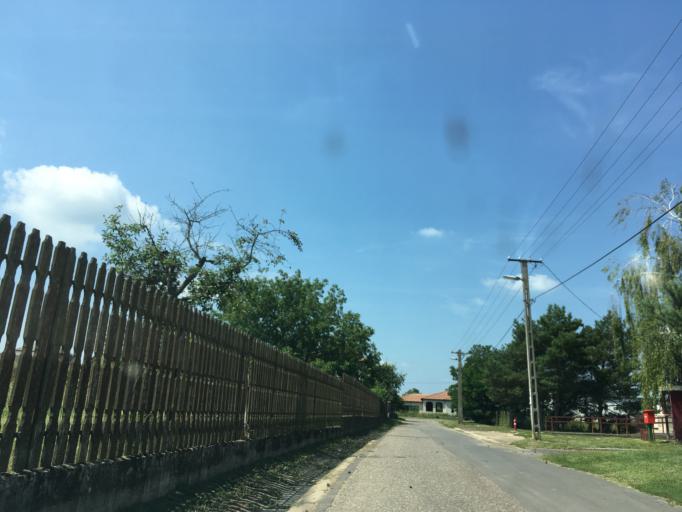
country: HU
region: Szabolcs-Szatmar-Bereg
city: Nyirbeltek
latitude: 47.6960
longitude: 22.1261
